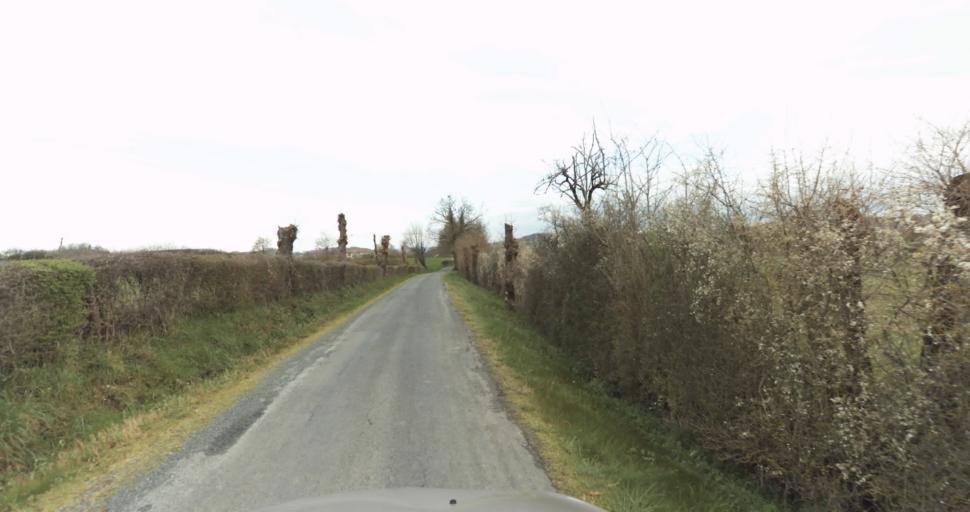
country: FR
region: Midi-Pyrenees
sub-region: Departement du Tarn
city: Frejairolles
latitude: 43.8740
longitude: 2.2041
